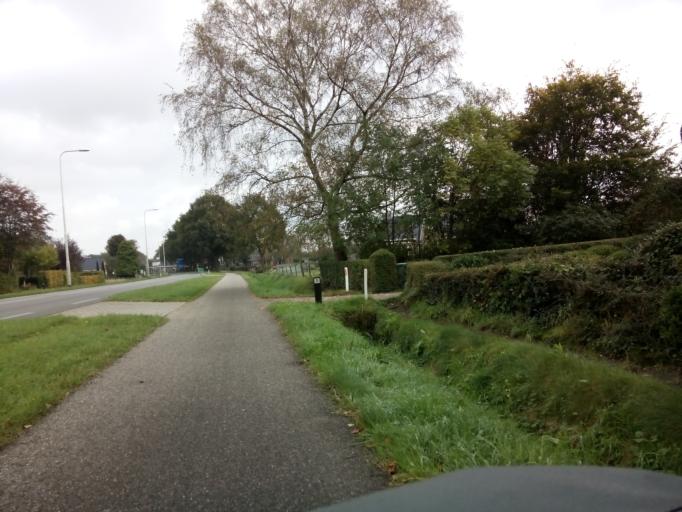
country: NL
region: Gelderland
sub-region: Gemeente Putten
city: Putten
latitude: 52.2558
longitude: 5.5827
